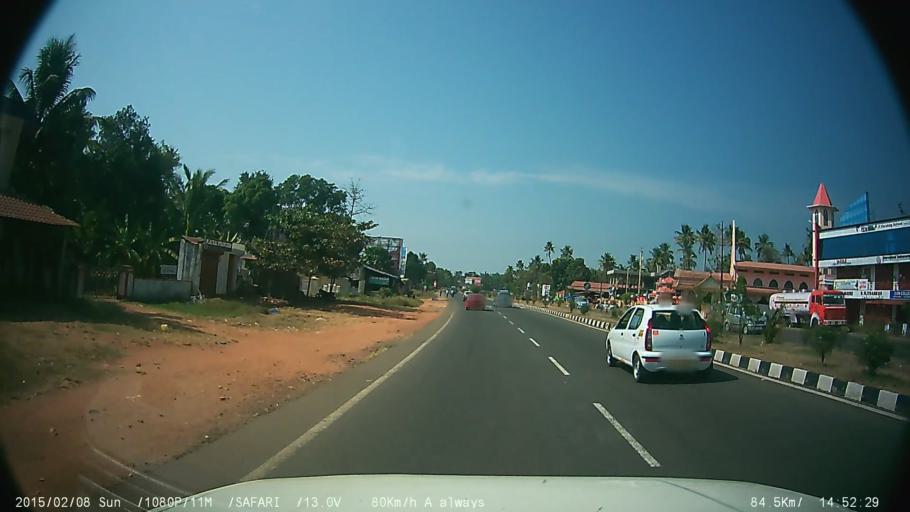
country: IN
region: Kerala
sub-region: Thrissur District
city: Kizhake Chalakudi
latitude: 10.2732
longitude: 76.3470
